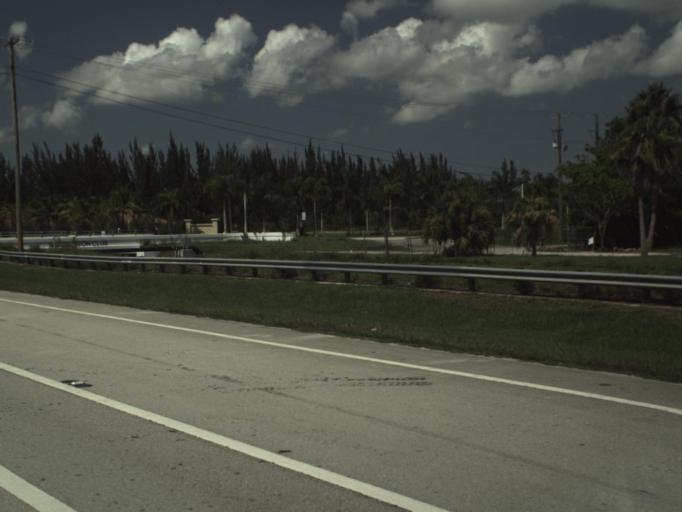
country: US
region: Florida
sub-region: Palm Beach County
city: Wellington
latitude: 26.5979
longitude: -80.2055
